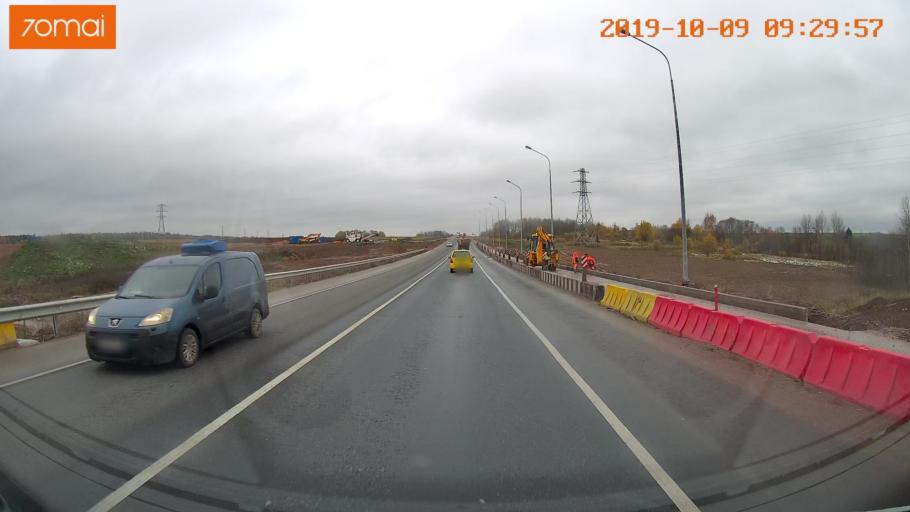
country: RU
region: Vologda
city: Vologda
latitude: 59.1359
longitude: 39.9535
